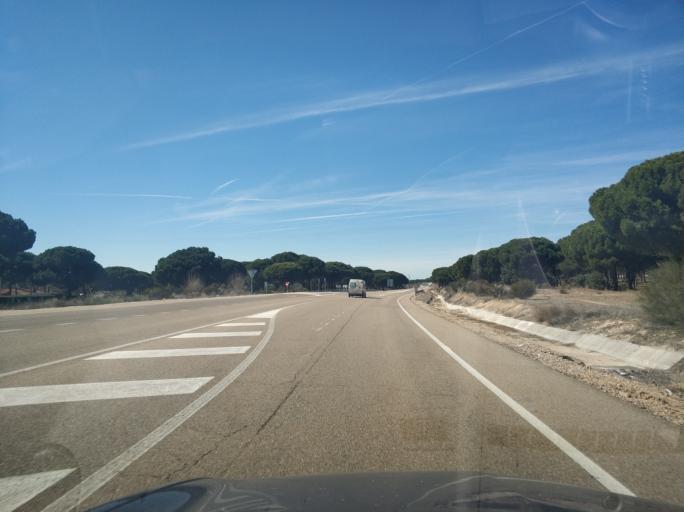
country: ES
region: Castille and Leon
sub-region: Provincia de Valladolid
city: Viana de Cega
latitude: 41.5322
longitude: -4.7275
